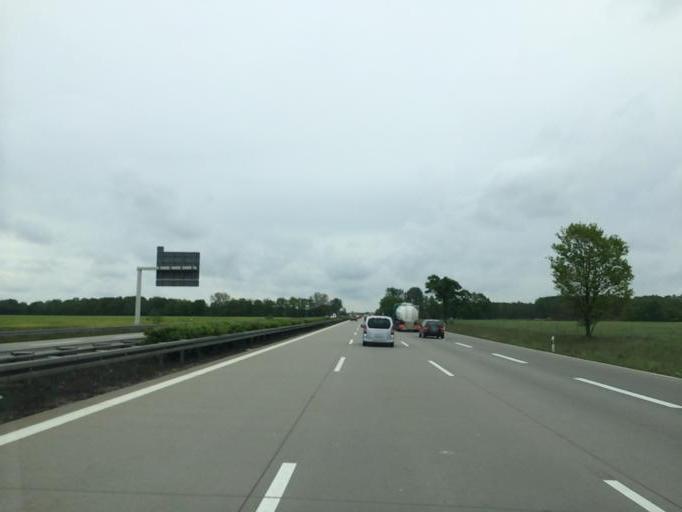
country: DE
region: Brandenburg
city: Ziesar
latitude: 52.2540
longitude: 12.3148
